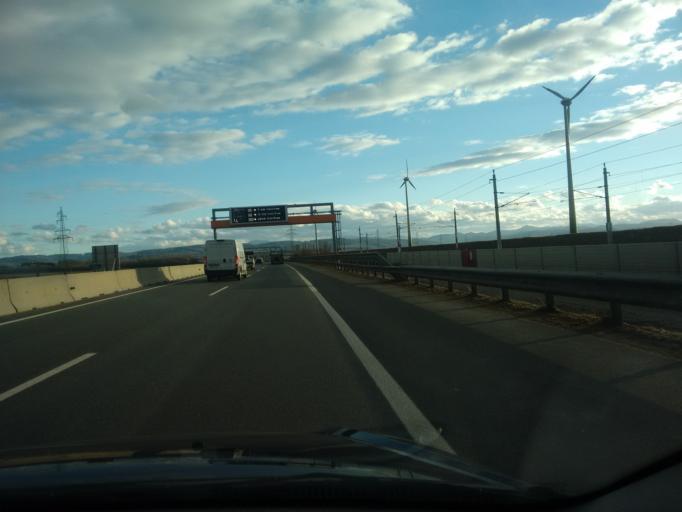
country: AT
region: Lower Austria
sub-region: Sankt Polten Stadt
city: Sankt Poelten
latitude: 48.1935
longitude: 15.6601
